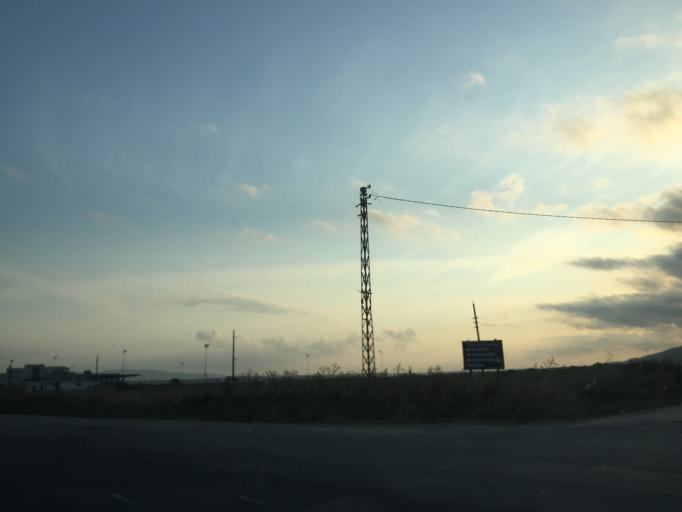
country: TR
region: Balikesir
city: Gonen
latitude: 40.0966
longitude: 27.6749
